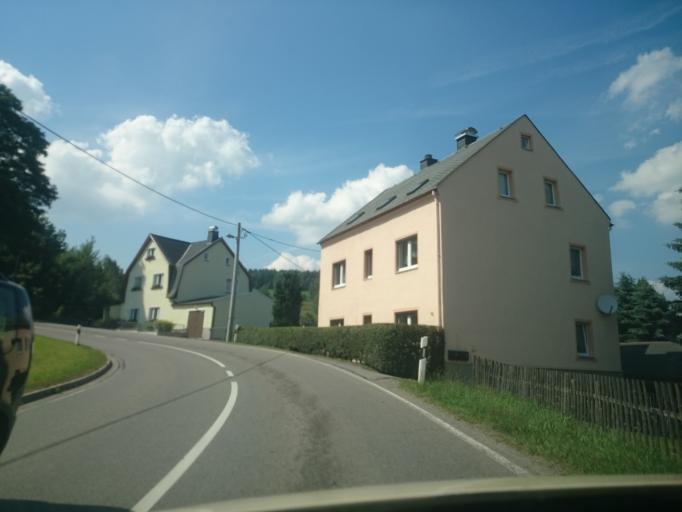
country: DE
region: Saxony
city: Pockau
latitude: 50.7103
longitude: 13.2192
